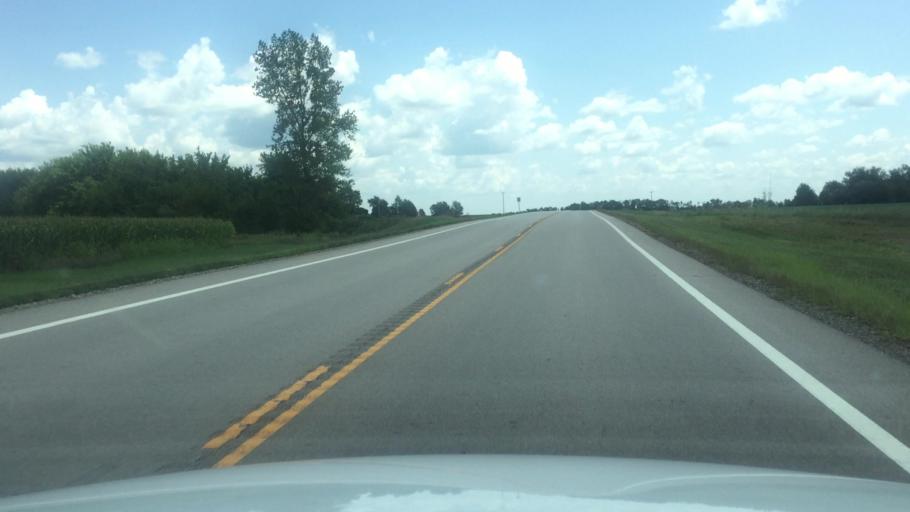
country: US
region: Kansas
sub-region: Brown County
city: Horton
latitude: 39.6661
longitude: -95.4188
